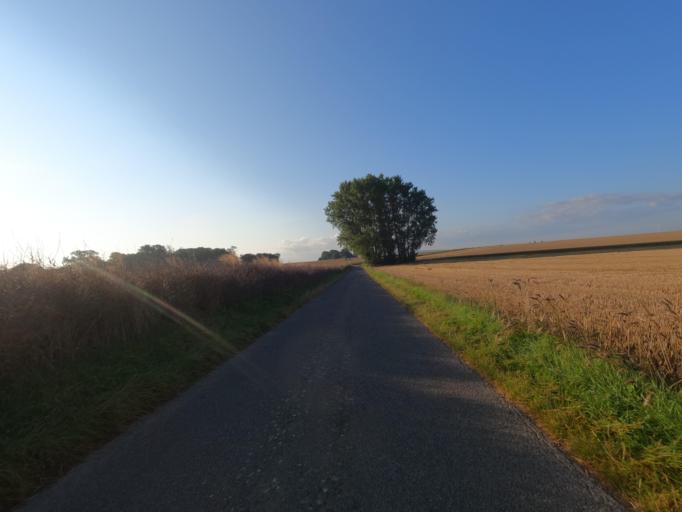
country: DE
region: North Rhine-Westphalia
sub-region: Regierungsbezirk Koln
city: Titz
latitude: 51.0175
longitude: 6.3606
